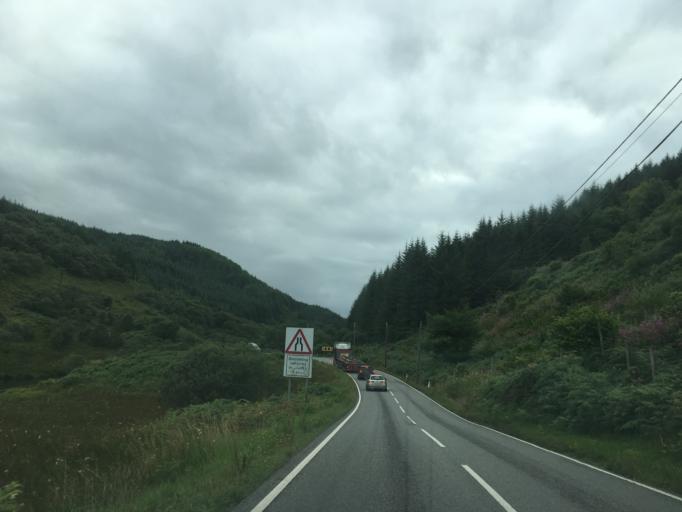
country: GB
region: Scotland
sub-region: Argyll and Bute
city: Oban
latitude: 56.2942
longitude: -5.4675
